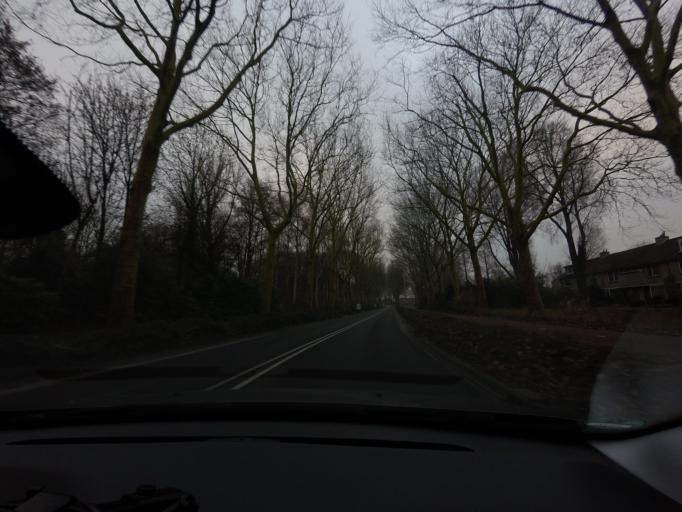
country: NL
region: South Holland
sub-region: Gemeente Barendrecht
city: Barendrecht
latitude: 51.8522
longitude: 4.5404
